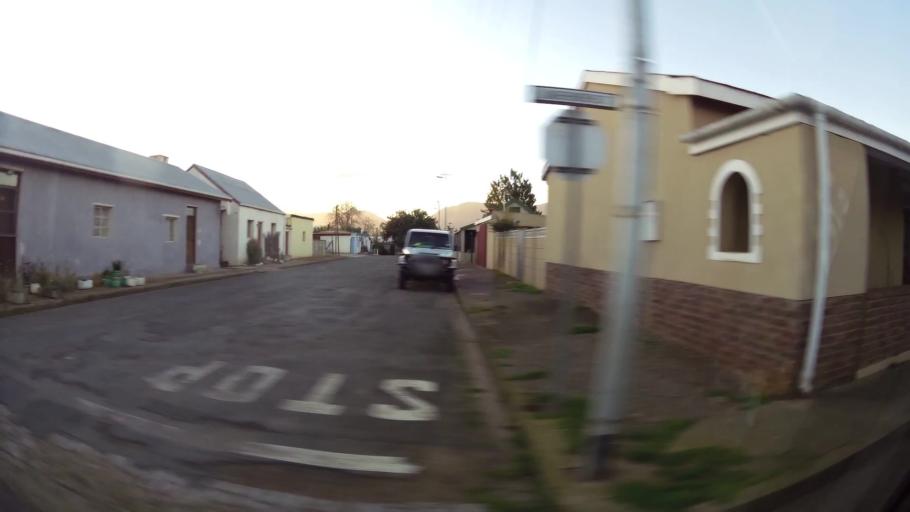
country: ZA
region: Western Cape
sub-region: Eden District Municipality
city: Riversdale
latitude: -34.0880
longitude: 21.2606
